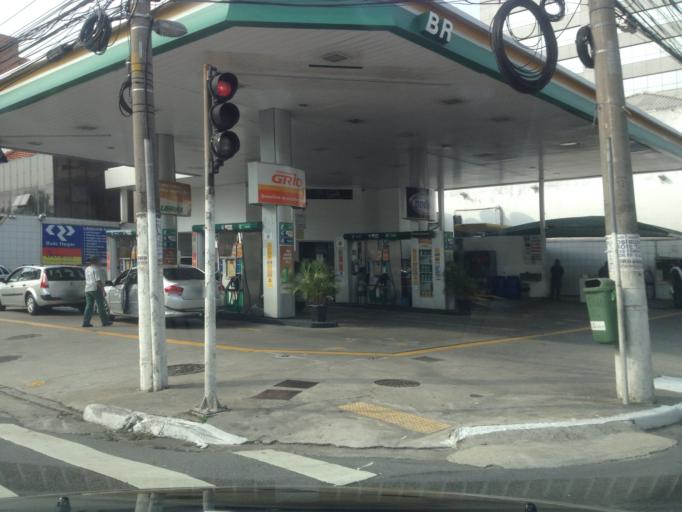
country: BR
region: Sao Paulo
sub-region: Sao Paulo
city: Sao Paulo
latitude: -23.5762
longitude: -46.6582
